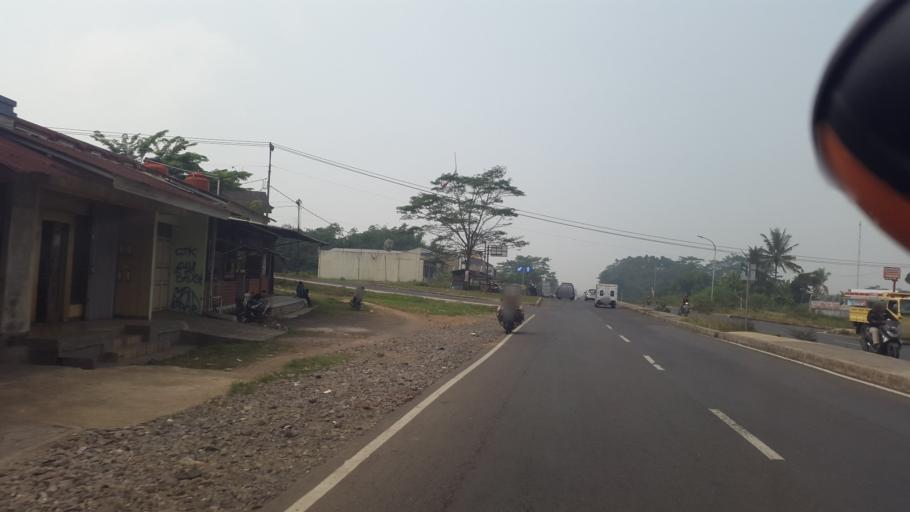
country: ID
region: West Java
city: Sukabumi
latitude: -6.9297
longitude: 106.8995
